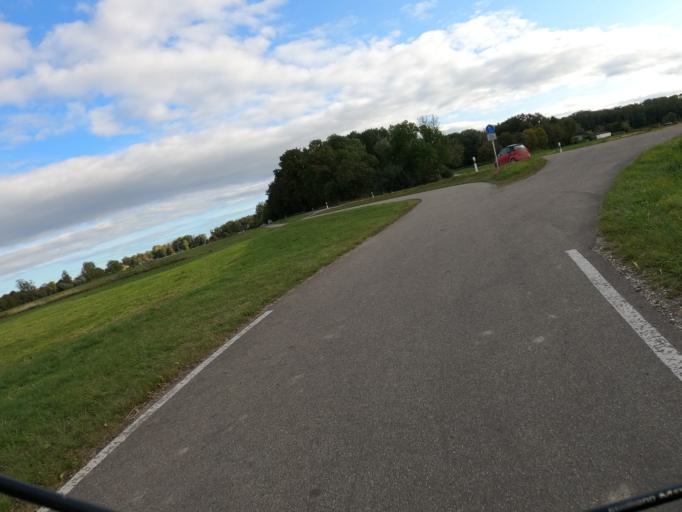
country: DE
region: Bavaria
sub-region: Swabia
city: Holzheim
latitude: 48.4008
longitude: 10.0953
